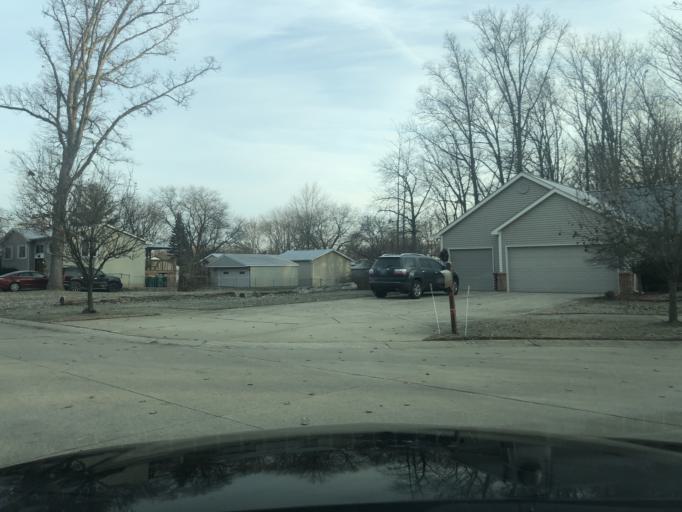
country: US
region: Michigan
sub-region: Wayne County
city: Romulus
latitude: 42.1876
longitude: -83.3350
